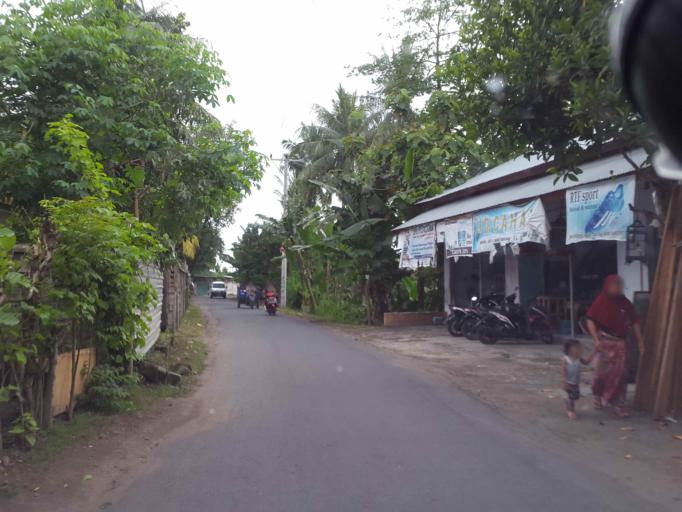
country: ID
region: West Nusa Tenggara
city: Mambalan
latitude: -8.5451
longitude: 116.1130
